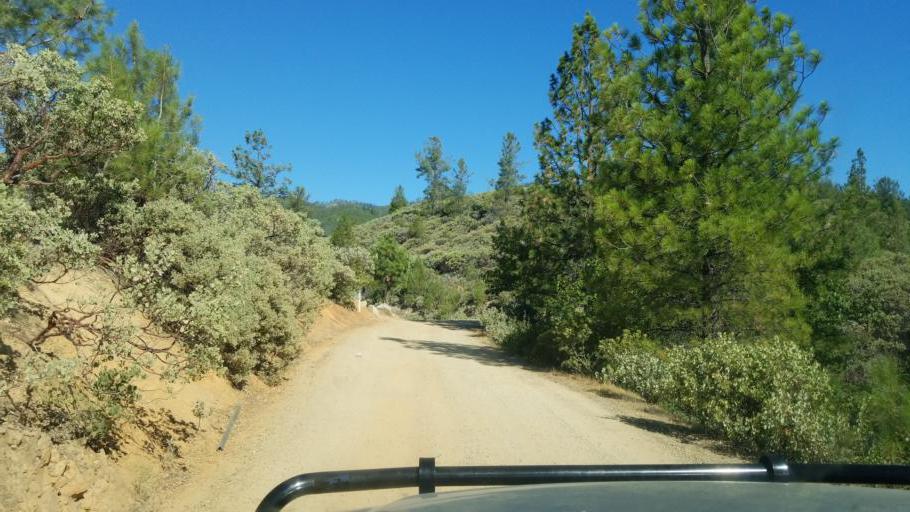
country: US
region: California
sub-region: Shasta County
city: Shasta
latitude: 40.6596
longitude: -122.4663
